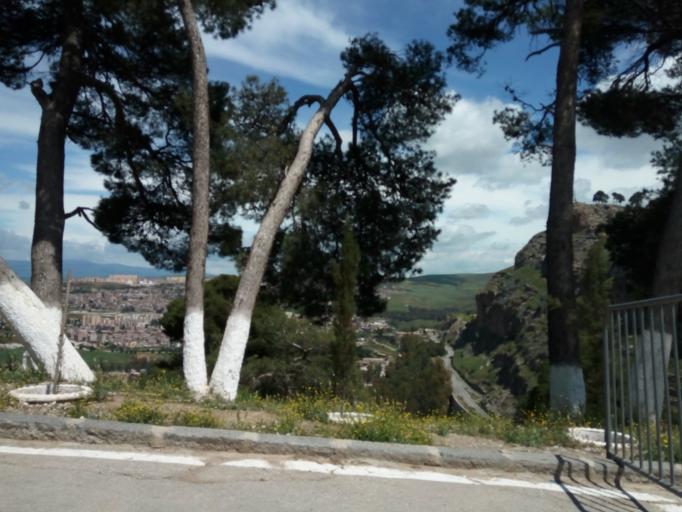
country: DZ
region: Constantine
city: Constantine
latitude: 36.3734
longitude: 6.6146
